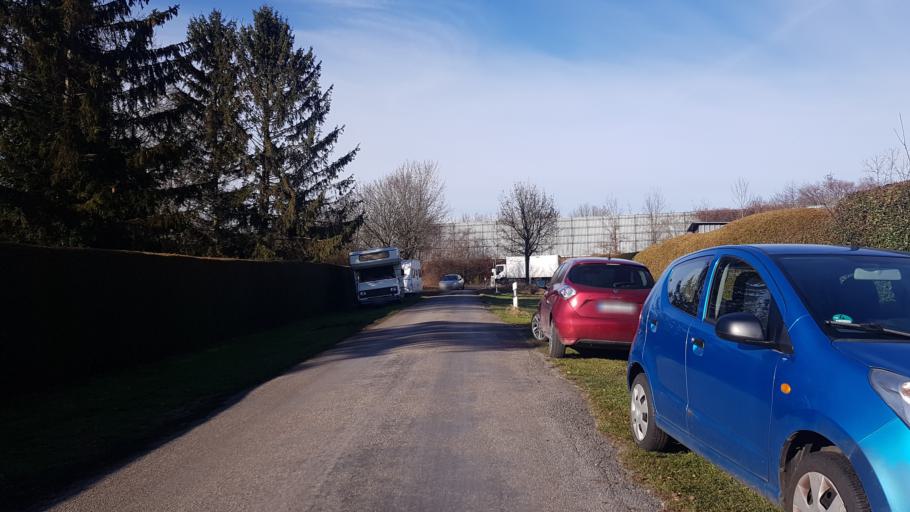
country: DE
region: Bavaria
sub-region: Upper Bavaria
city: Karlsfeld
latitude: 48.2204
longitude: 11.5177
